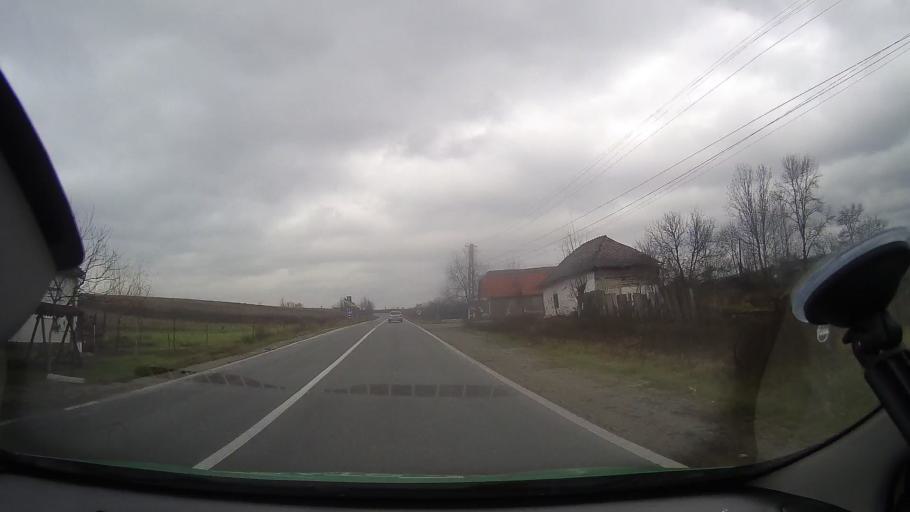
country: RO
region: Arad
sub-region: Comuna Almas
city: Almas
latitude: 46.2837
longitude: 22.2408
